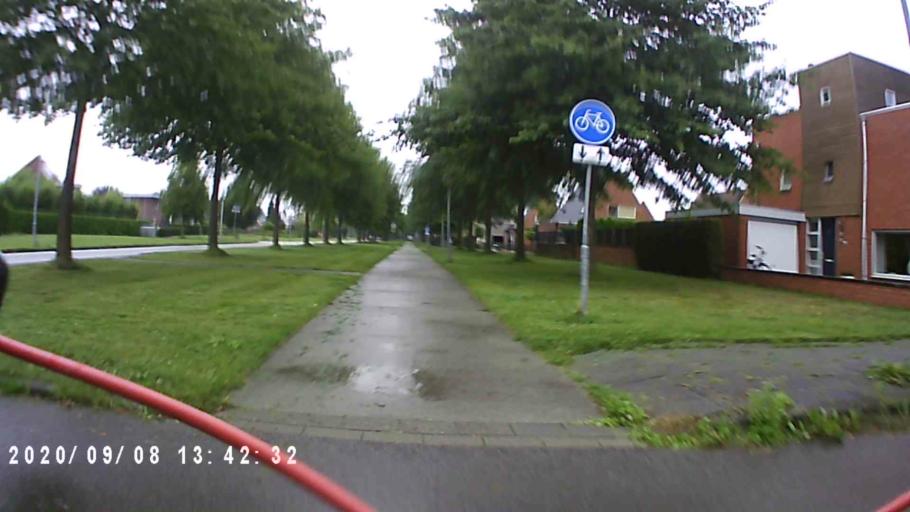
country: NL
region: Groningen
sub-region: Gemeente Veendam
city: Veendam
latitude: 53.1154
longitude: 6.8639
